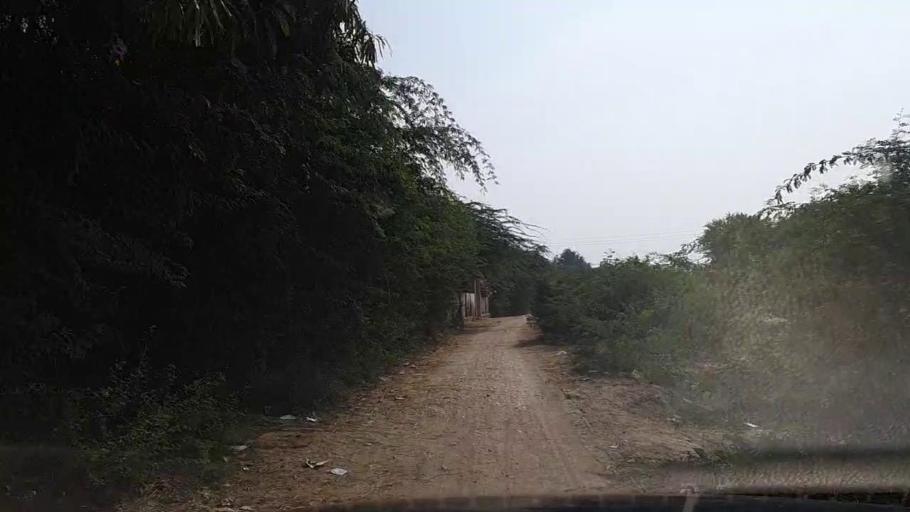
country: PK
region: Sindh
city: Mirpur Batoro
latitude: 24.6972
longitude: 68.2191
